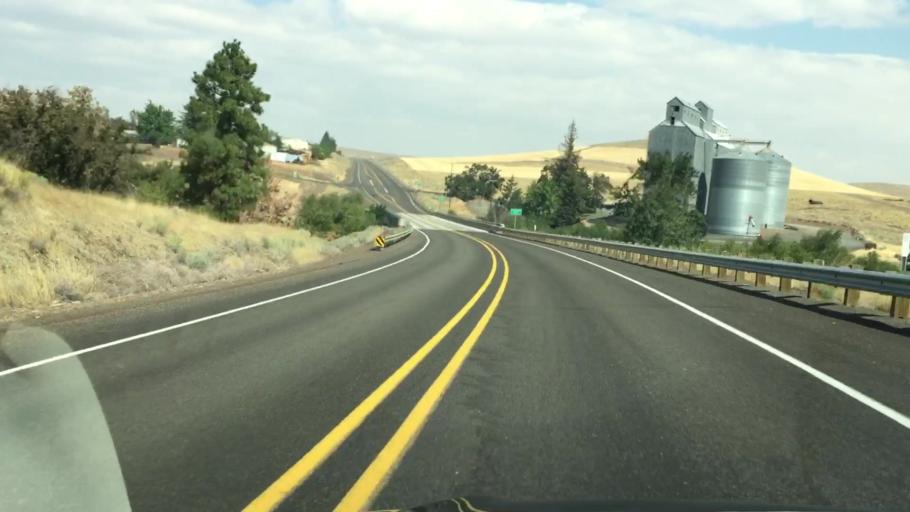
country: US
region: Oregon
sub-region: Wasco County
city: The Dalles
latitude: 45.4492
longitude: -121.1191
